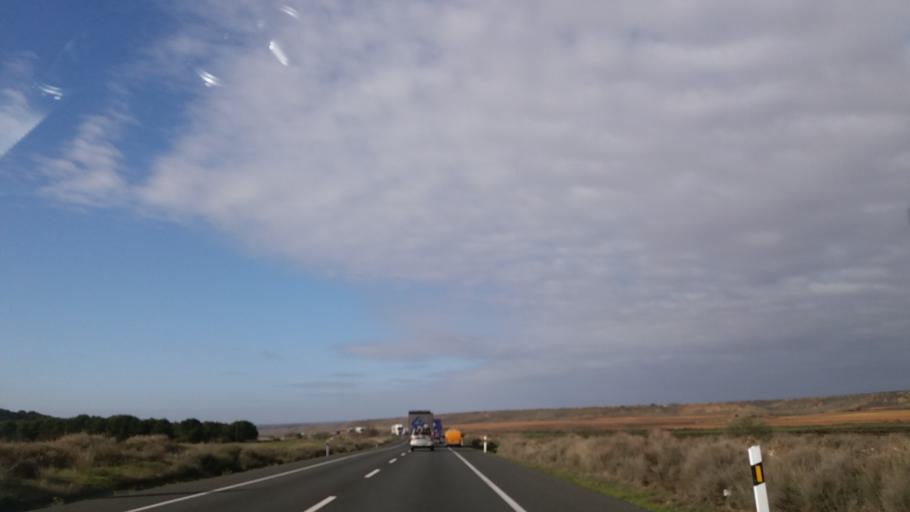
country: ES
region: Aragon
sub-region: Provincia de Huesca
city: Ballobar
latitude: 41.5209
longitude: 0.1961
